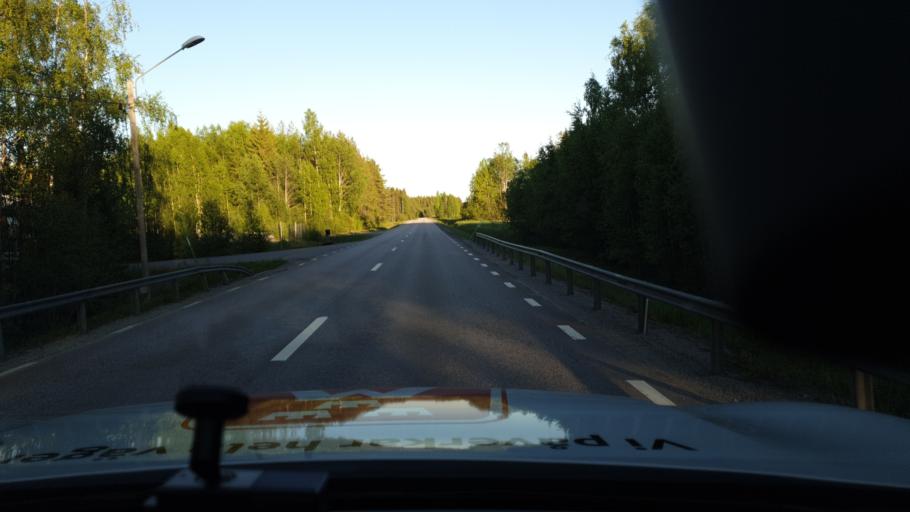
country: SE
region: Vaesterbotten
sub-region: Umea Kommun
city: Ersmark
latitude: 63.9795
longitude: 20.2590
